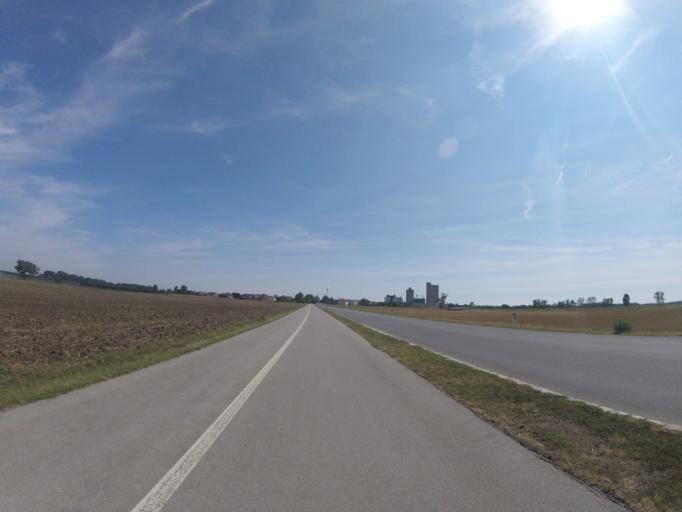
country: AT
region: Burgenland
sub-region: Politischer Bezirk Neusiedl am See
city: Sankt Andra am Zicksee
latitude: 47.7841
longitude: 16.9197
